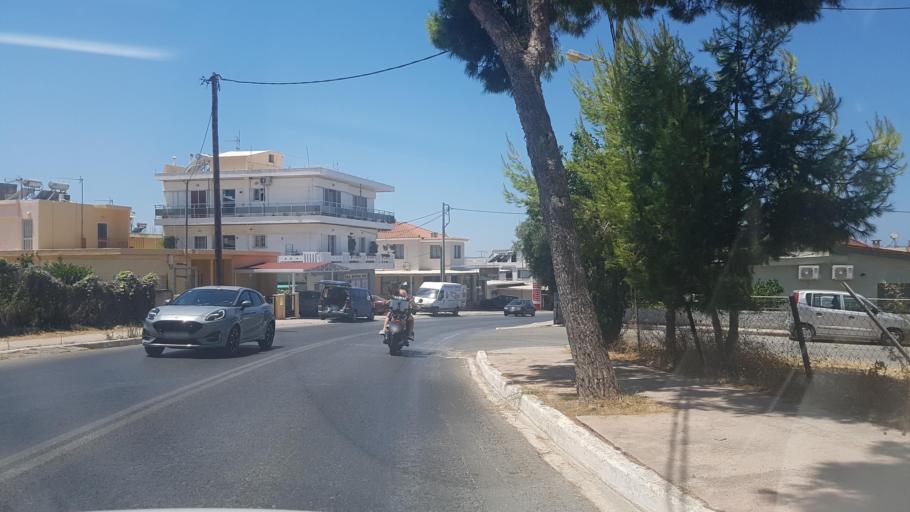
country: GR
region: Crete
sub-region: Nomos Chanias
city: Chania
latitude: 35.5131
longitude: 24.0490
